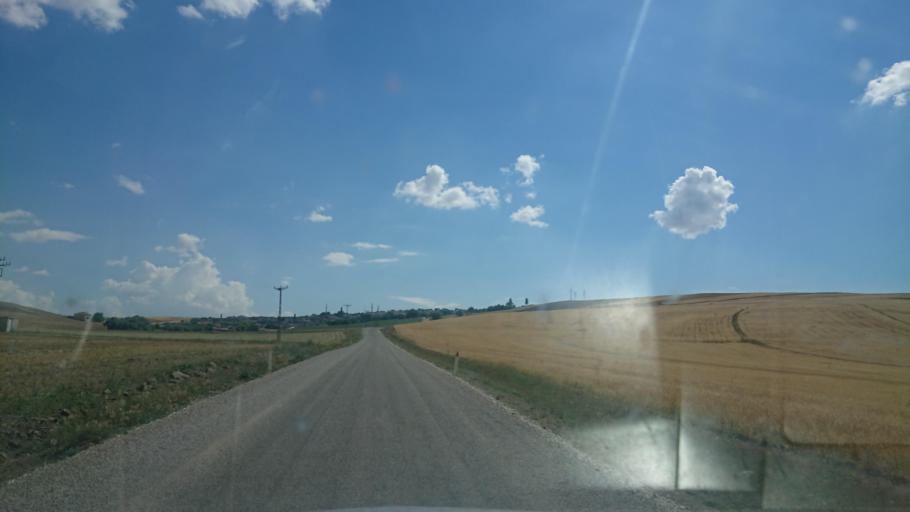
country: TR
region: Aksaray
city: Agacoren
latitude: 38.7802
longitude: 33.7933
